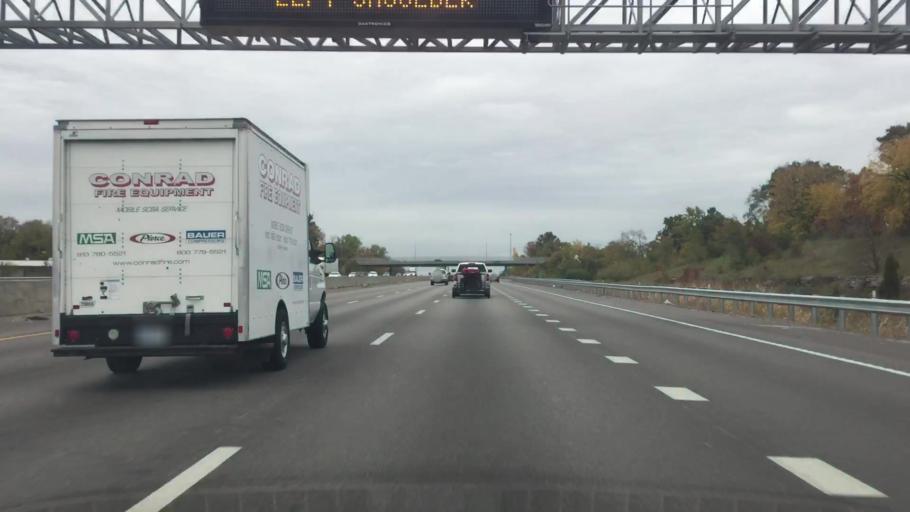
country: US
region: Missouri
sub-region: Jackson County
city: Raytown
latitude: 39.0321
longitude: -94.5003
